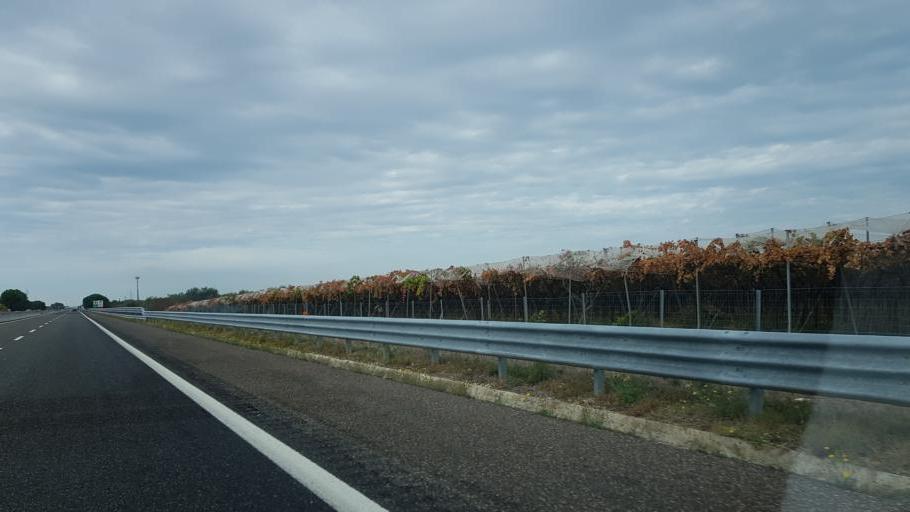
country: IT
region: Apulia
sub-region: Provincia di Barletta - Andria - Trani
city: Bisceglie
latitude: 41.1891
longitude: 16.5042
